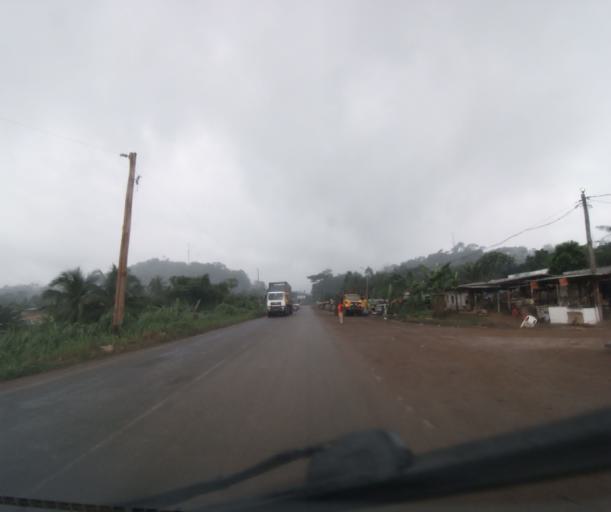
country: CM
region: Centre
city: Eseka
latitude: 3.8886
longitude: 10.7115
